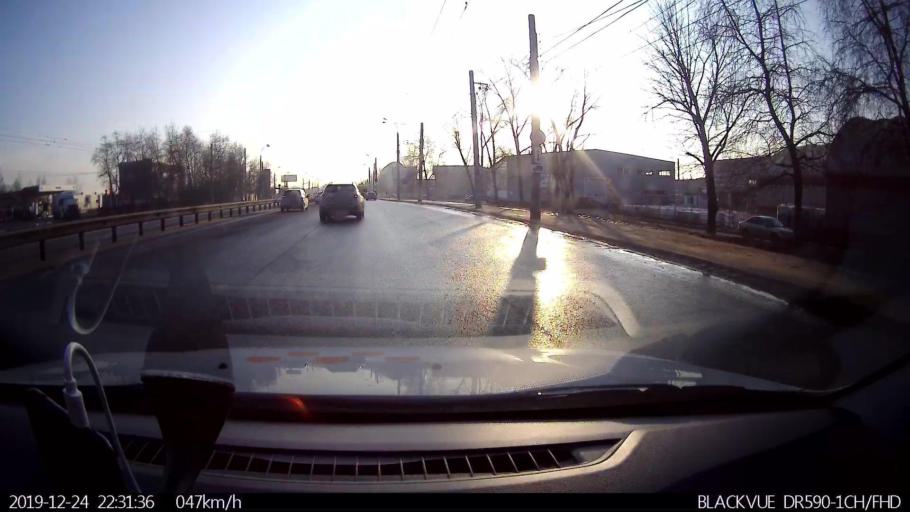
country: RU
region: Nizjnij Novgorod
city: Nizhniy Novgorod
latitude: 56.3103
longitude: 43.8692
